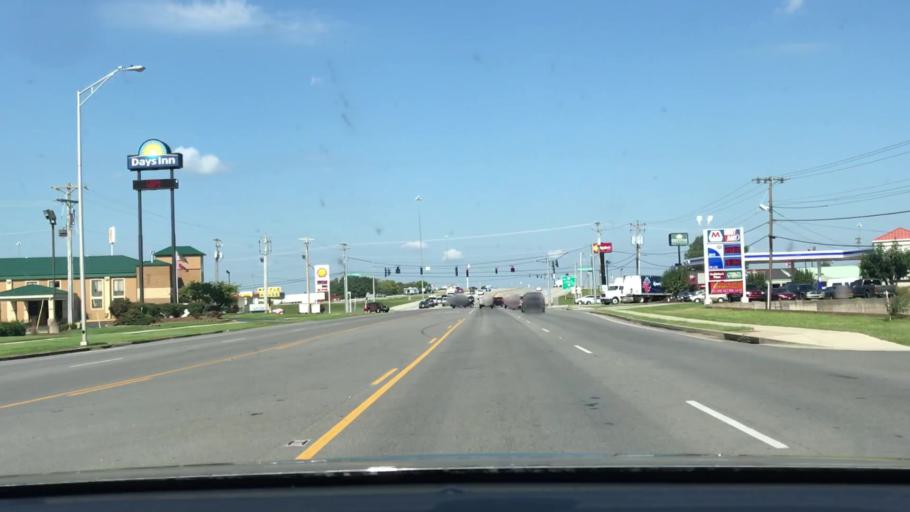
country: US
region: Kentucky
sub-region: Warren County
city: Plano
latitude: 36.9315
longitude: -86.4148
